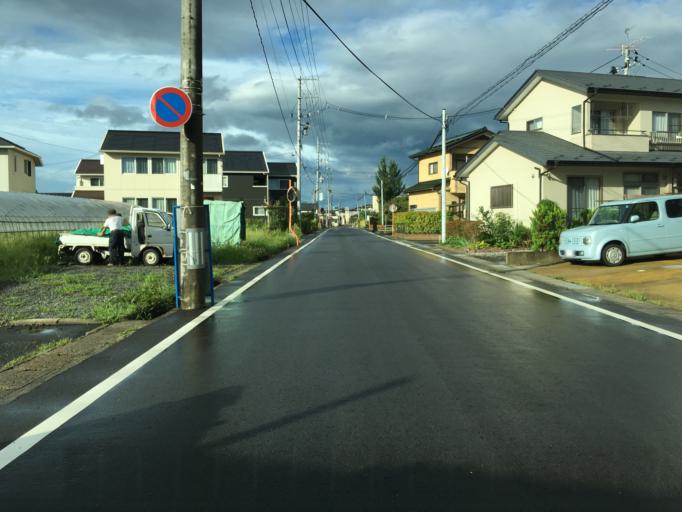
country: JP
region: Fukushima
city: Fukushima-shi
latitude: 37.7185
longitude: 140.4493
